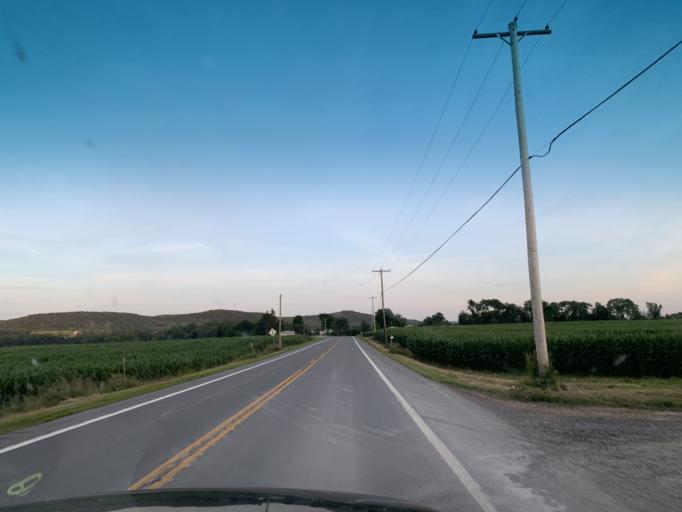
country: US
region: New York
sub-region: Oneida County
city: Chadwicks
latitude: 42.9166
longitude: -75.2428
